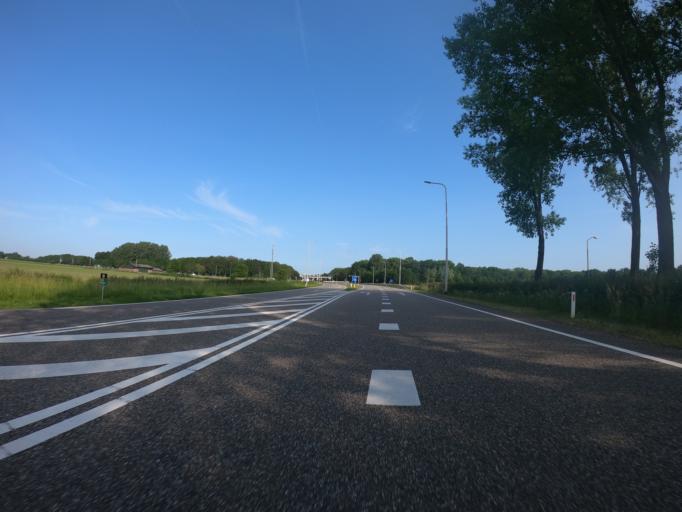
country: NL
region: North Brabant
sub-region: Gemeente Landerd
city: Reek
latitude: 51.7869
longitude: 5.6623
